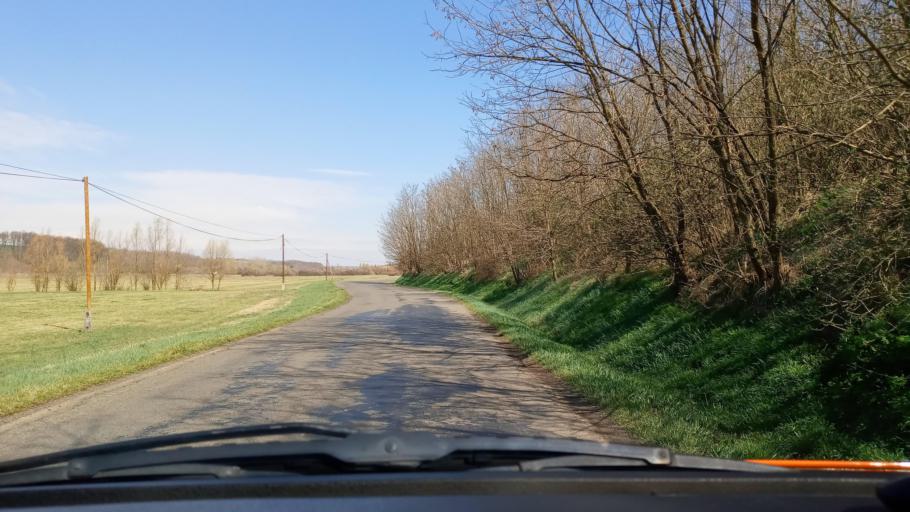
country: HU
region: Baranya
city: Pecsvarad
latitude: 46.0607
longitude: 18.4588
